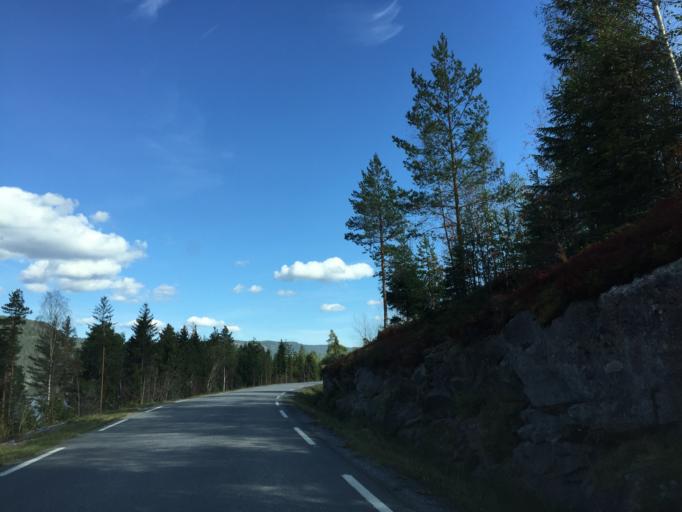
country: NO
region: Buskerud
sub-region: Ovre Eiker
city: Hokksund
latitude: 59.6628
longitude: 9.8921
